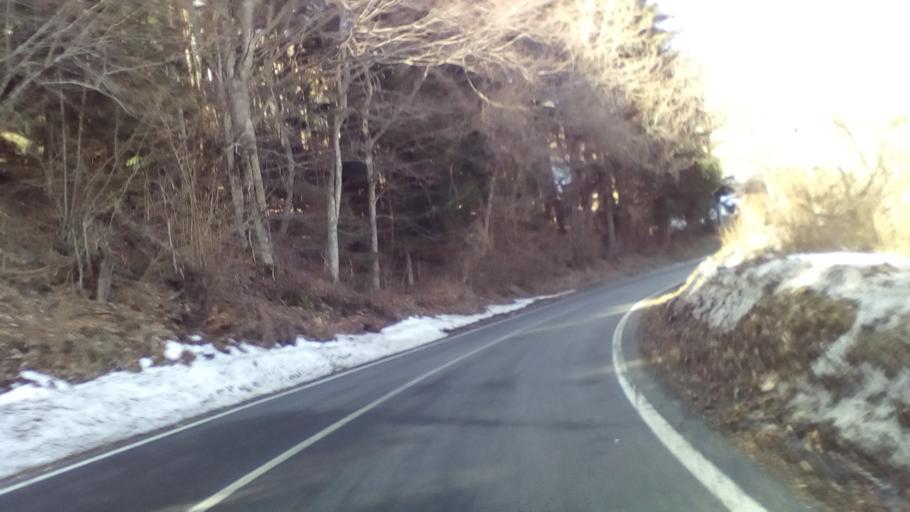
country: IT
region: Emilia-Romagna
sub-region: Provincia di Modena
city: Riolunato
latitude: 44.2606
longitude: 10.6484
